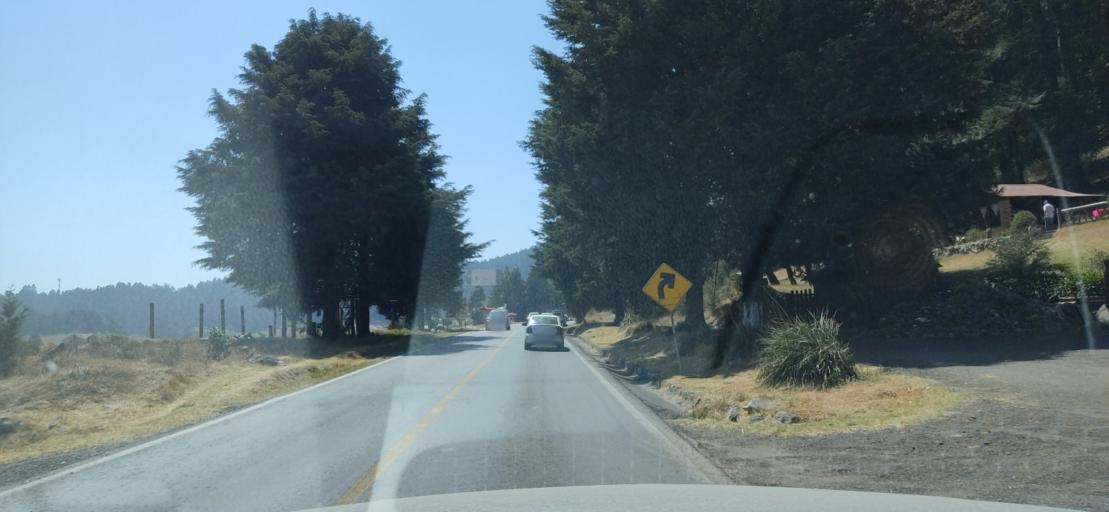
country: MX
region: Mexico
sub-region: Ocoyoacac
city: San Jeronimo Acazulco
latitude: 19.2844
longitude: -99.3750
